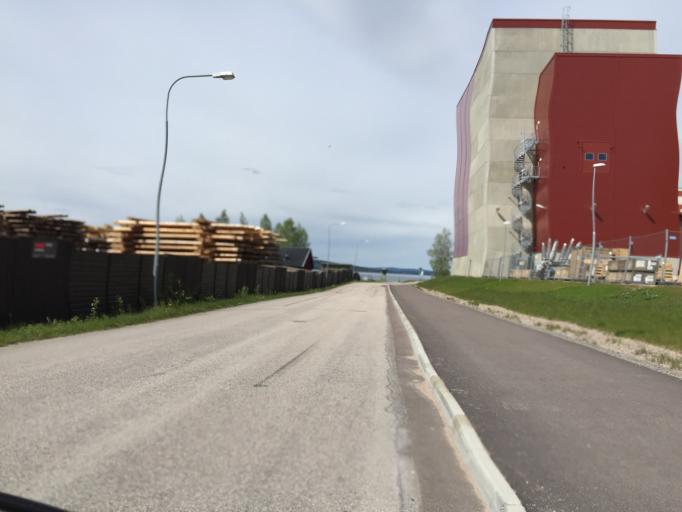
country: SE
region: Dalarna
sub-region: Ludvika Kommun
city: Ludvika
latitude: 60.1453
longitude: 15.1687
